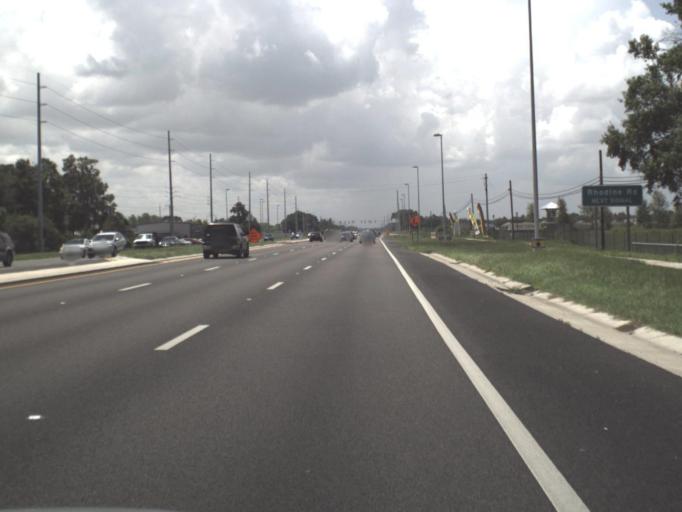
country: US
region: Florida
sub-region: Hillsborough County
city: Riverview
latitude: 27.8265
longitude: -82.3303
